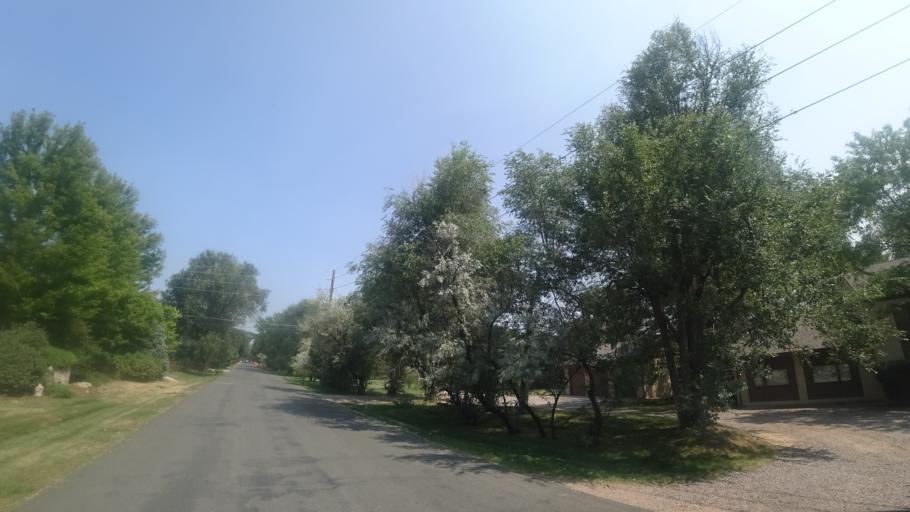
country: US
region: Colorado
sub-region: Arapahoe County
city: Englewood
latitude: 39.6296
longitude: -104.9778
